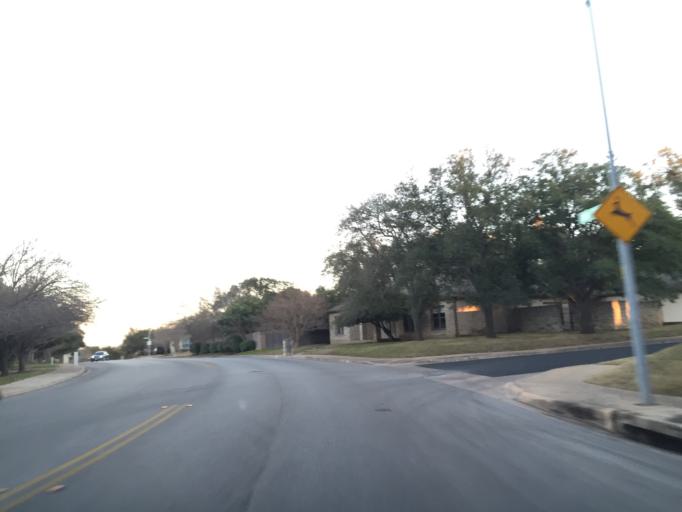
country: US
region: Texas
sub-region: Williamson County
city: Jollyville
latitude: 30.4103
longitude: -97.7664
